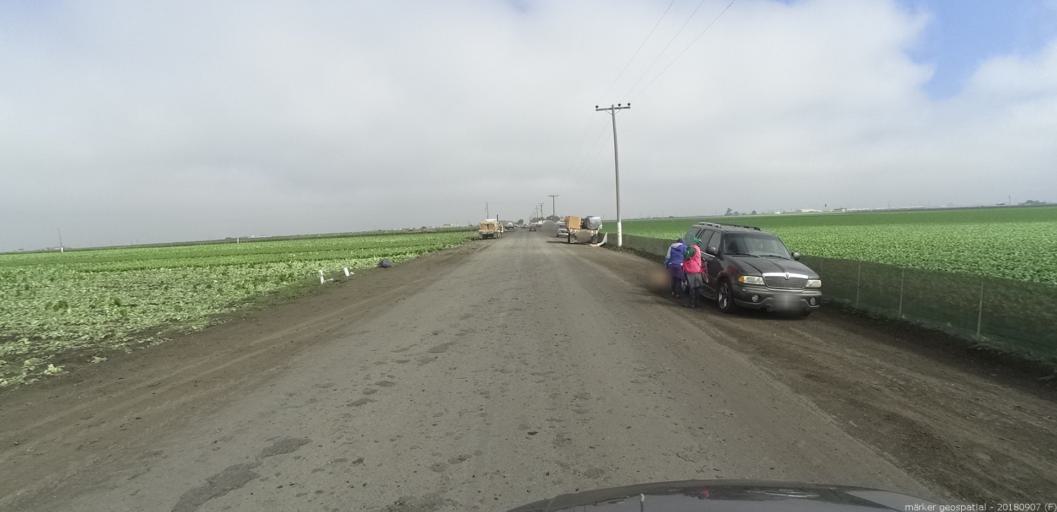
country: US
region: California
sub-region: Monterey County
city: Boronda
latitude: 36.6840
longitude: -121.7079
